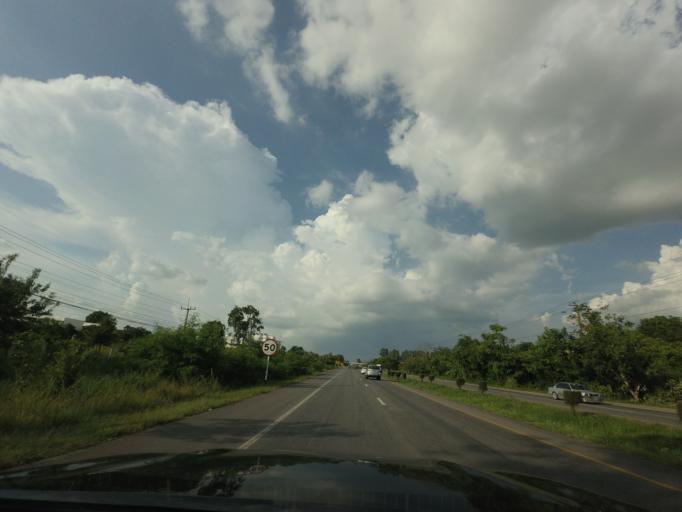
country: TH
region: Khon Kaen
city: Ban Haet
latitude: 16.2474
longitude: 102.7725
